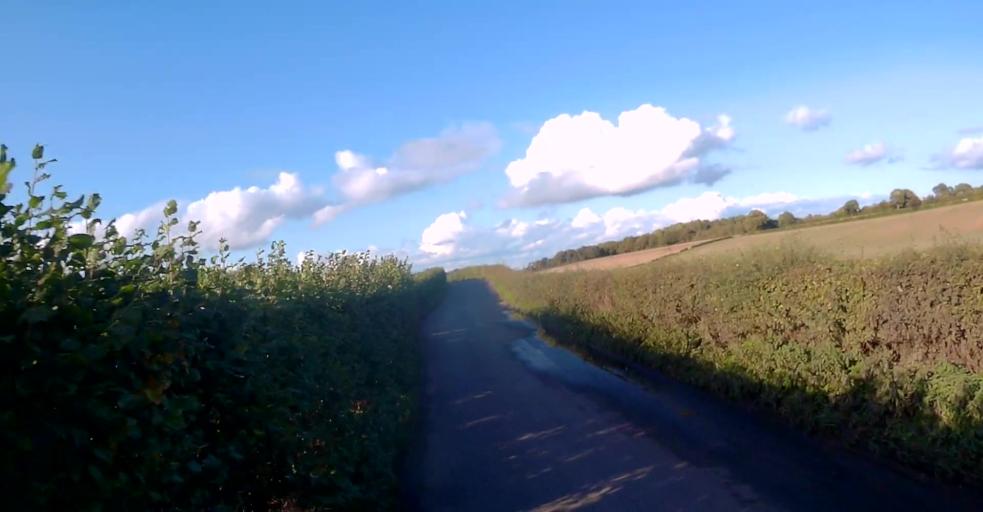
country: GB
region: England
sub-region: Hampshire
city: Long Sutton
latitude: 51.2266
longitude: -0.9236
